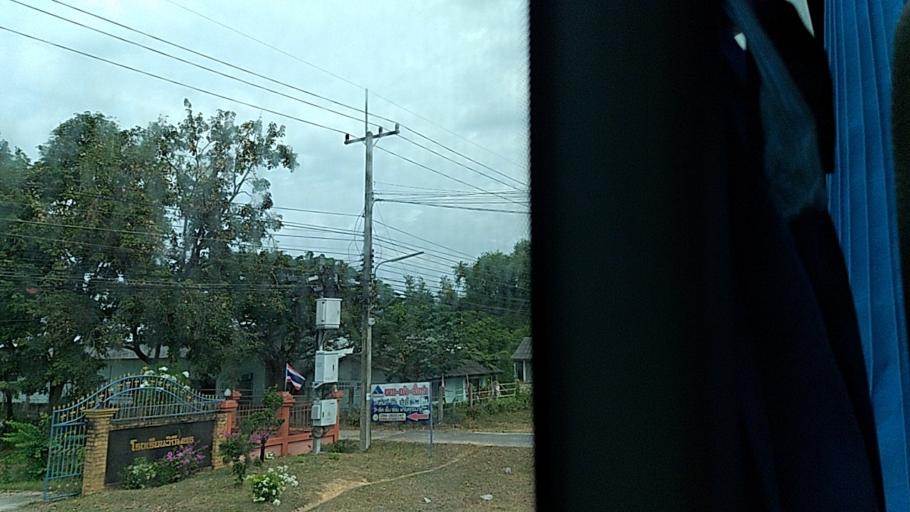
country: TH
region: Maha Sarakham
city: Maha Sarakham
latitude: 16.1482
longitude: 103.4011
